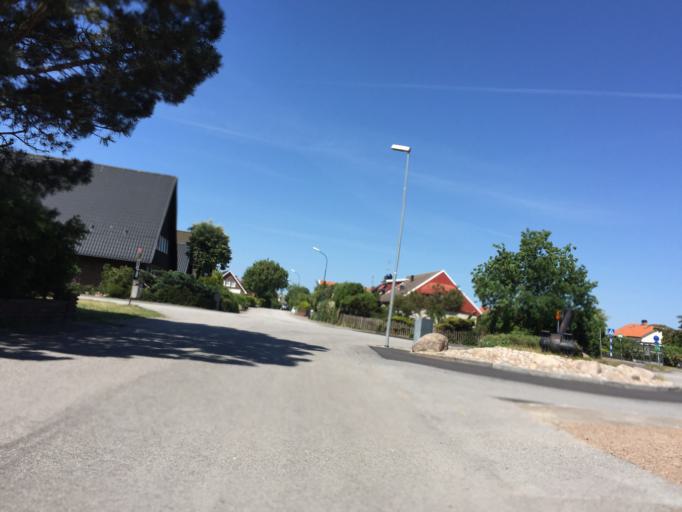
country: SE
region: Skane
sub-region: Trelleborgs Kommun
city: Trelleborg
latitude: 55.3563
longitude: 13.2372
